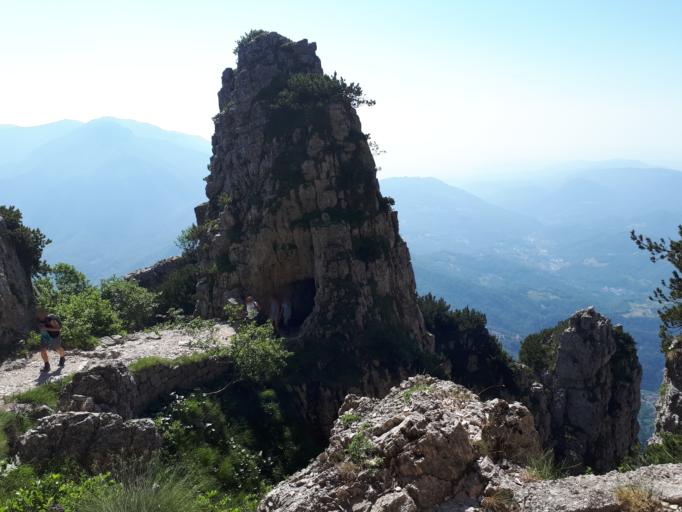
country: IT
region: Veneto
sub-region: Provincia di Vicenza
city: Posina
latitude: 45.7803
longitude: 11.2201
